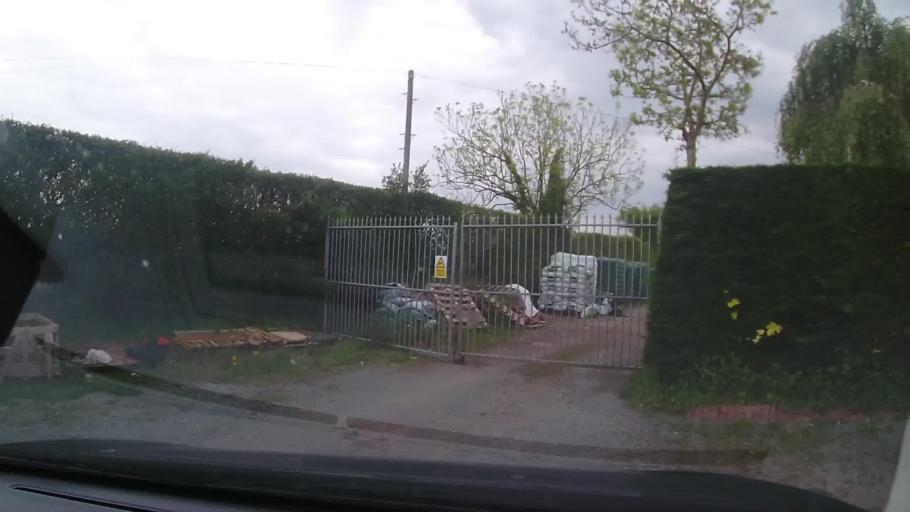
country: GB
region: Wales
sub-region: Wrexham
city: Overton
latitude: 52.9451
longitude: -2.9264
